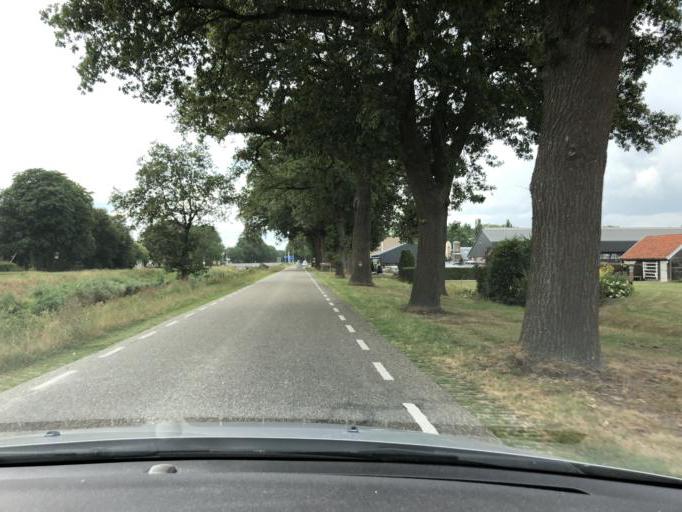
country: NL
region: Drenthe
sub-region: Gemeente Assen
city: Assen
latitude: 52.8651
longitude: 6.6386
